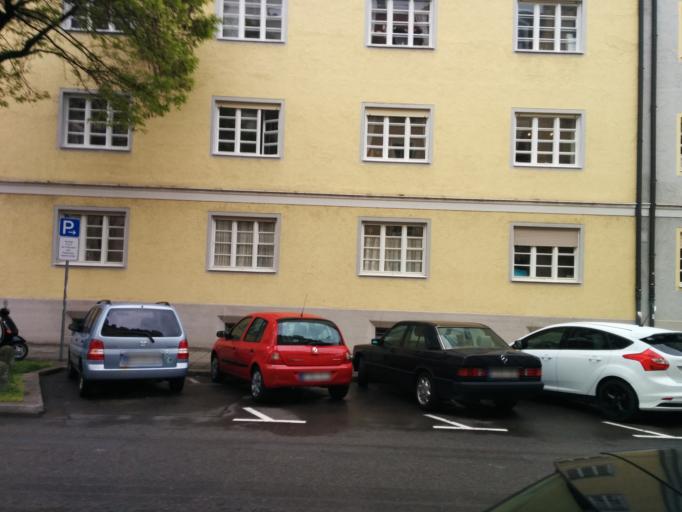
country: DE
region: Bavaria
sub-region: Upper Bavaria
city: Munich
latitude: 48.1636
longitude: 11.5765
